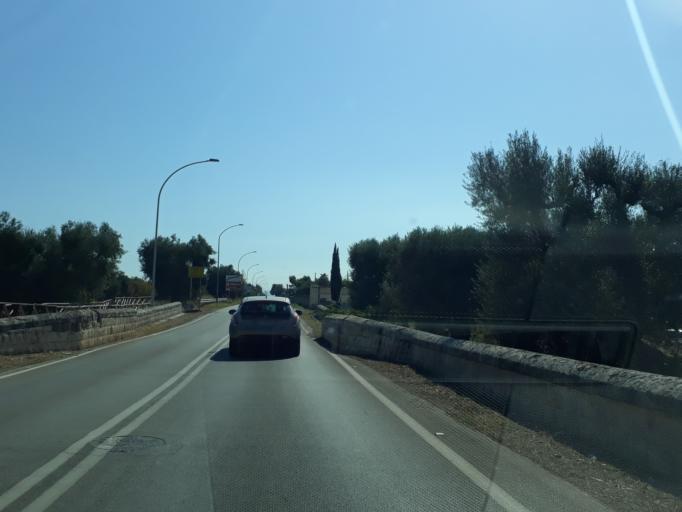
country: IT
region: Apulia
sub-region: Provincia di Bari
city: Monopoli
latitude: 40.9358
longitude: 17.3092
